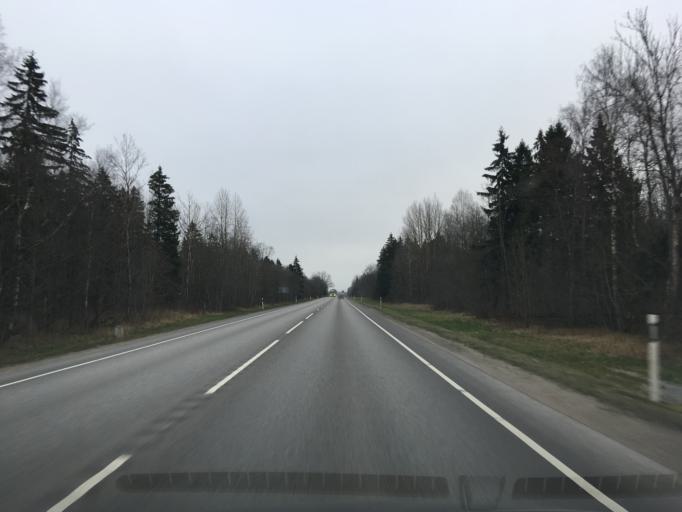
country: EE
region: Ida-Virumaa
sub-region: Kohtla-Jaerve linn
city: Kohtla-Jarve
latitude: 59.4179
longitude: 27.2879
